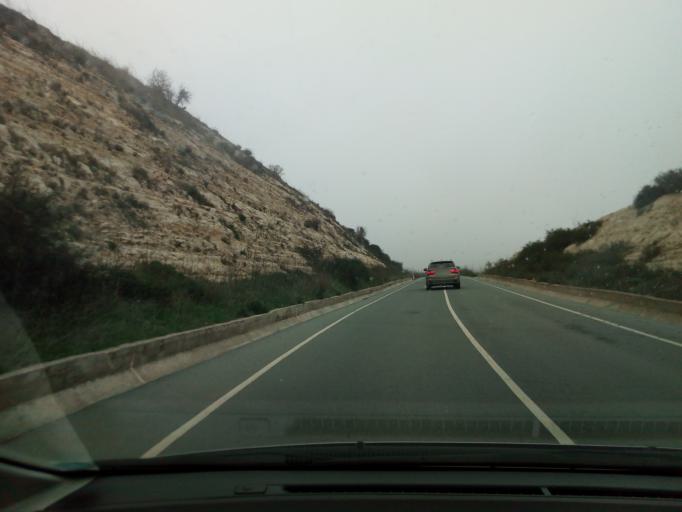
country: CY
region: Pafos
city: Pegeia
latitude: 34.9037
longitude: 32.4426
